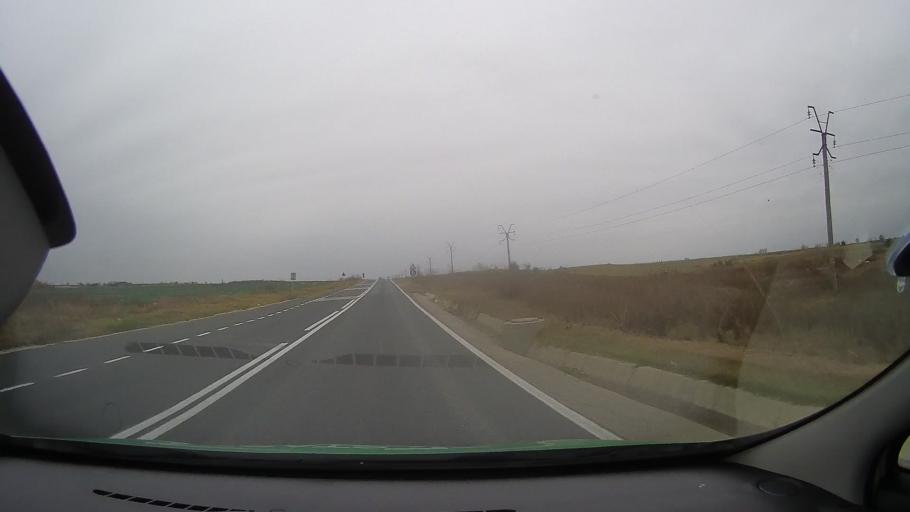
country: RO
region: Constanta
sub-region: Oras Harsova
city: Harsova
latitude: 44.6923
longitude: 27.9392
